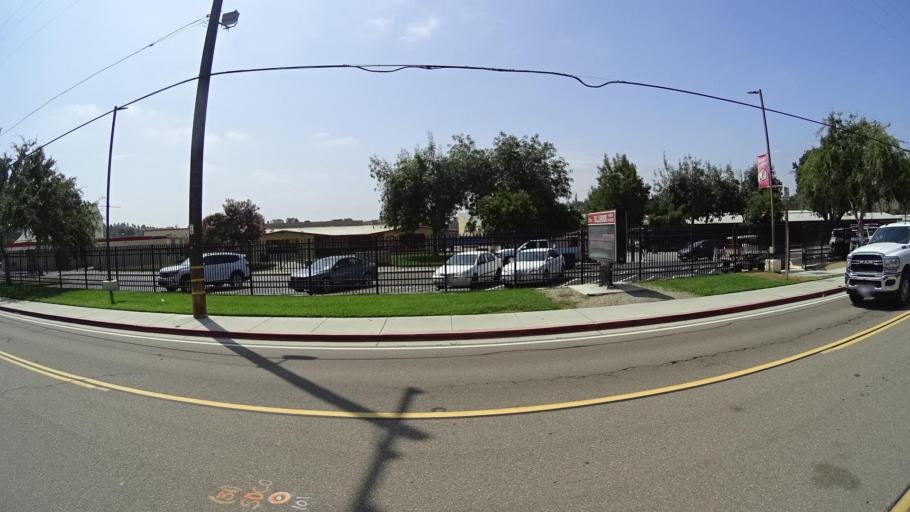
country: US
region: California
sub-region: San Diego County
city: Fallbrook
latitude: 33.3495
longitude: -117.2413
